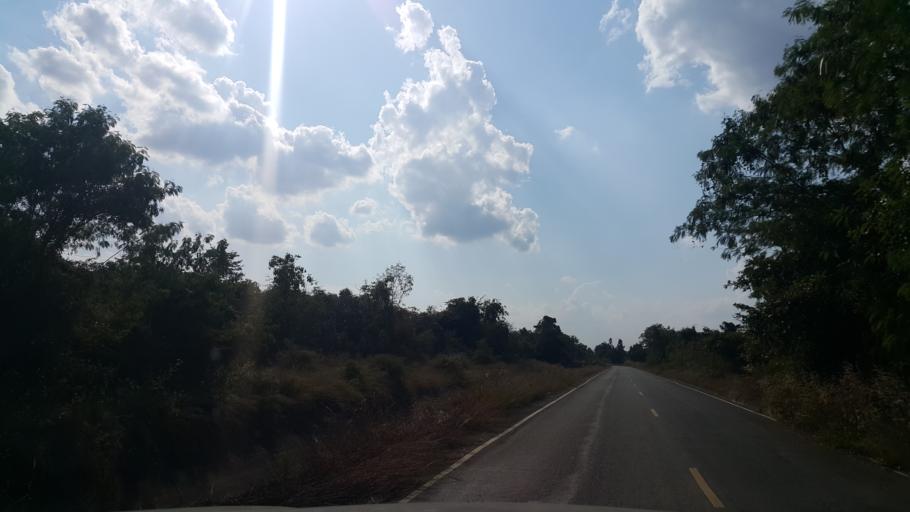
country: TH
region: Lamphun
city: Ban Thi
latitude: 18.5643
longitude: 99.1146
